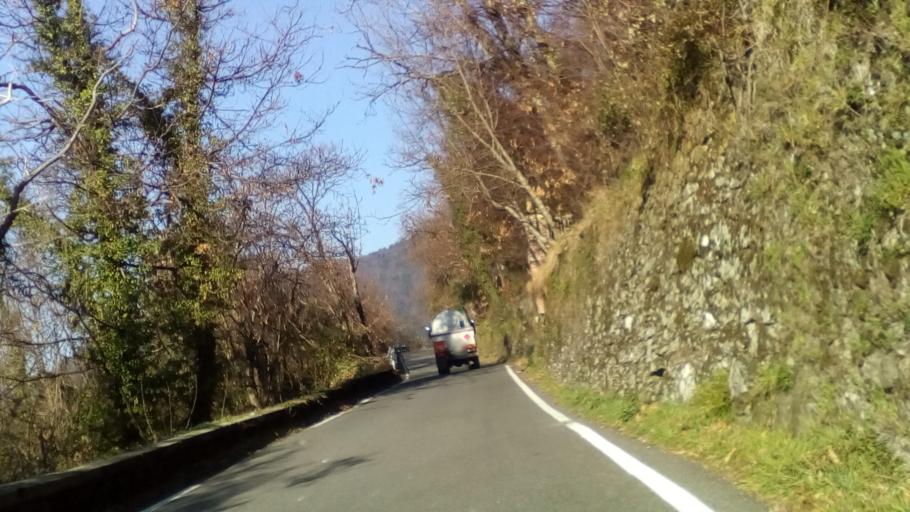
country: IT
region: Tuscany
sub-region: Provincia di Massa-Carrara
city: Montignoso
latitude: 44.0543
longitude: 10.1861
